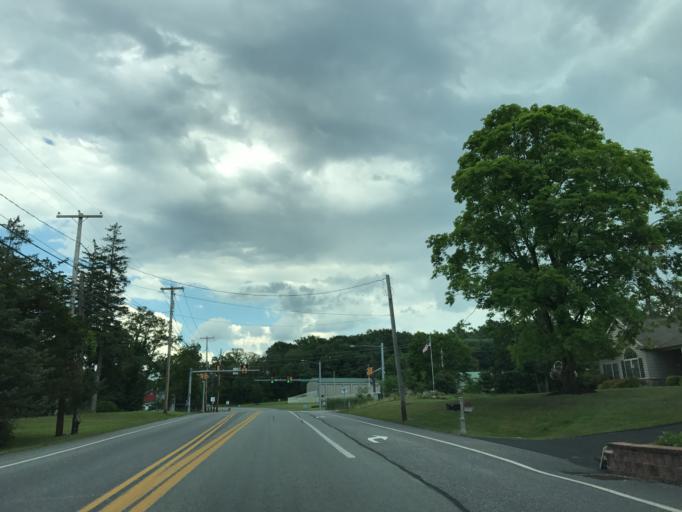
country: US
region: Pennsylvania
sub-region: Lancaster County
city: Elizabethtown
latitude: 40.1628
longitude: -76.6387
